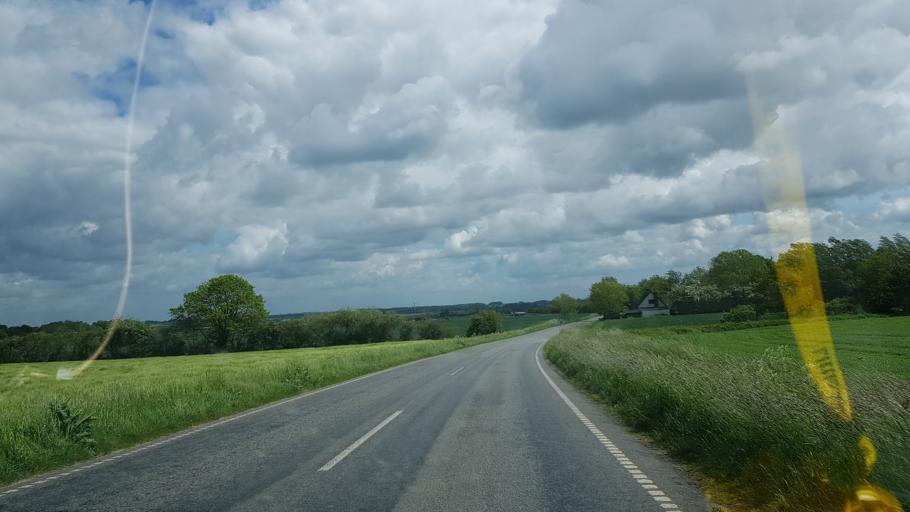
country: DK
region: South Denmark
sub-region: Kolding Kommune
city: Christiansfeld
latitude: 55.3325
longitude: 9.4316
